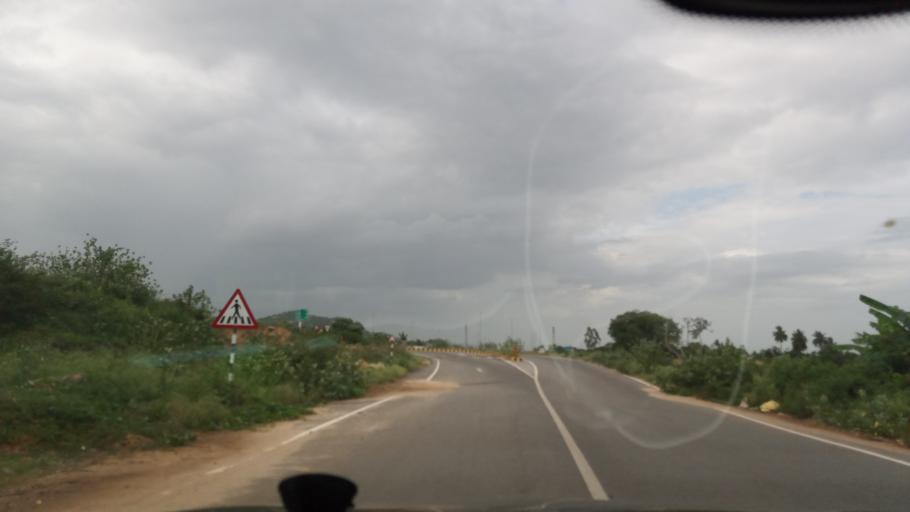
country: IN
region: Andhra Pradesh
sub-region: Chittoor
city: Palmaner
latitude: 13.1858
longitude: 78.8409
